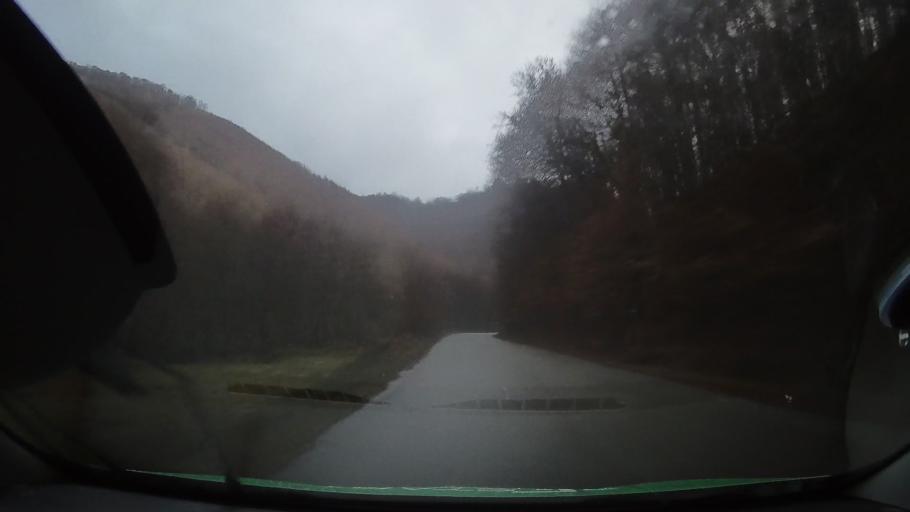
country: RO
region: Hunedoara
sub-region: Comuna Ribita
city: Ribita
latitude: 46.2809
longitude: 22.7370
